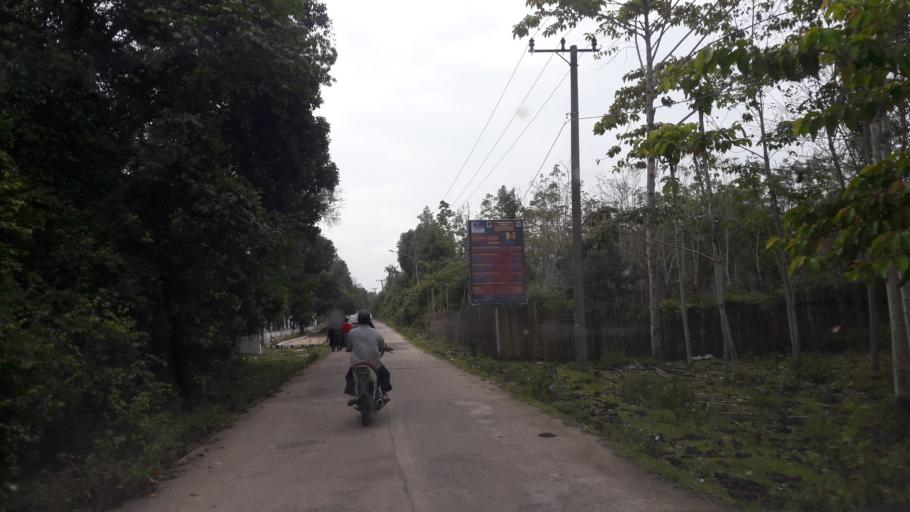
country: ID
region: South Sumatra
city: Gunungmenang
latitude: -3.1062
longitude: 104.0721
